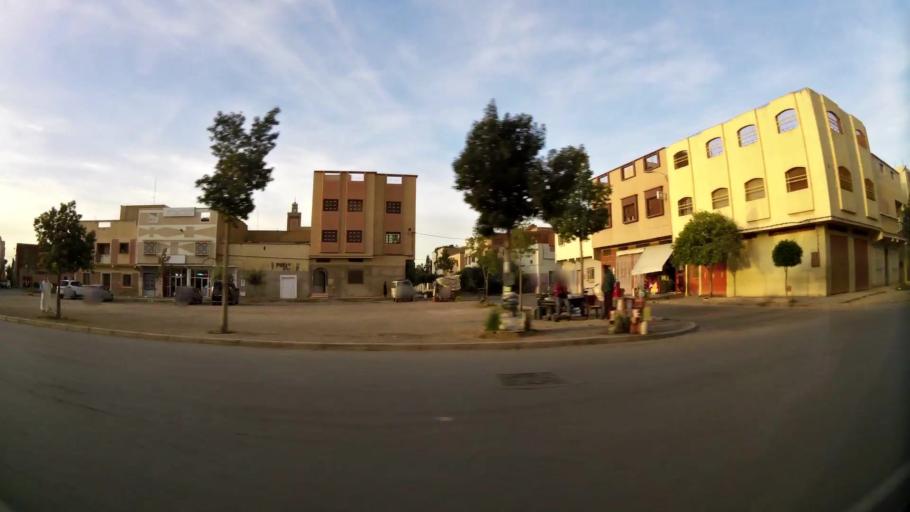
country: MA
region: Oriental
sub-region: Oujda-Angad
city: Oujda
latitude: 34.6776
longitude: -1.8872
